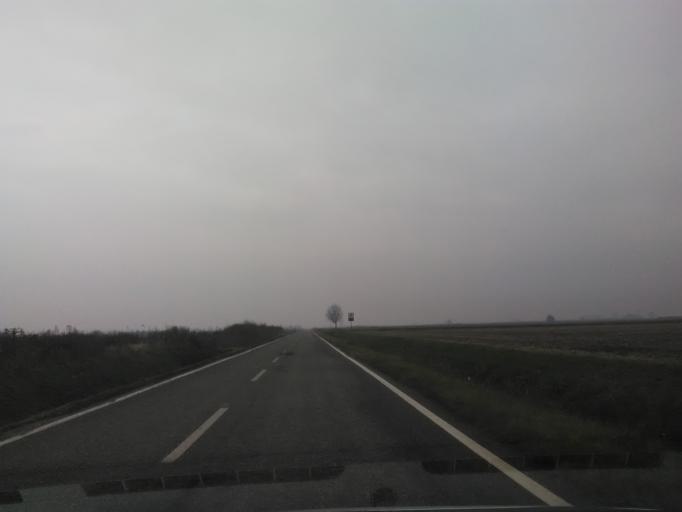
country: IT
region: Piedmont
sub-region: Provincia di Vercelli
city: Salasco
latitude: 45.3029
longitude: 8.2609
